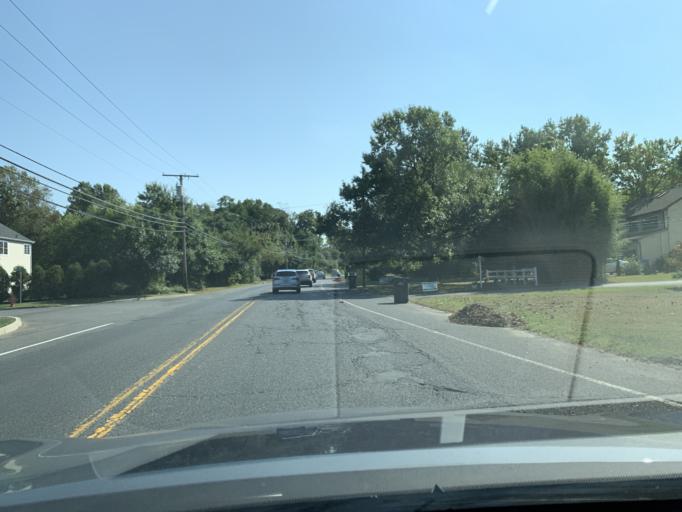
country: US
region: New Jersey
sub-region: Monmouth County
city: Tinton Falls
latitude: 40.2939
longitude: -74.0944
